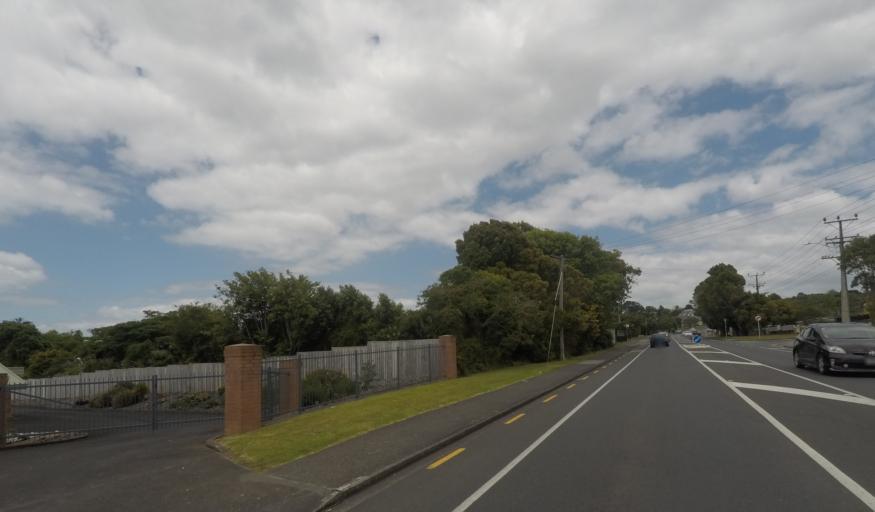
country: NZ
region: Auckland
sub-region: Auckland
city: Rosebank
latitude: -36.8264
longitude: 174.6078
